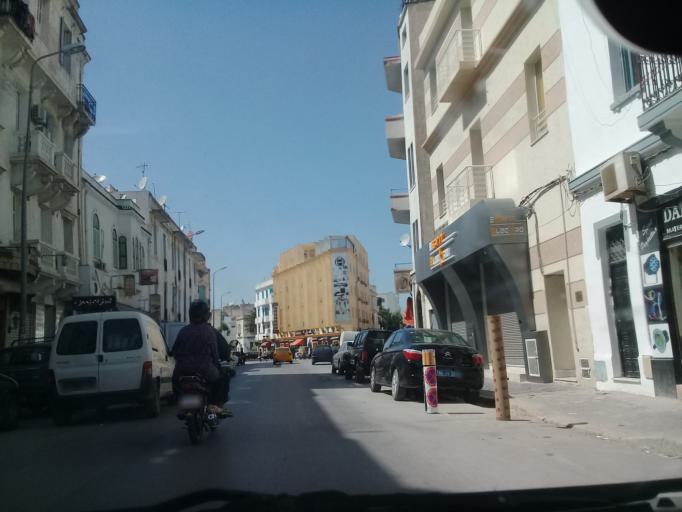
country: TN
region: Tunis
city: Tunis
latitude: 36.8090
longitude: 10.1791
